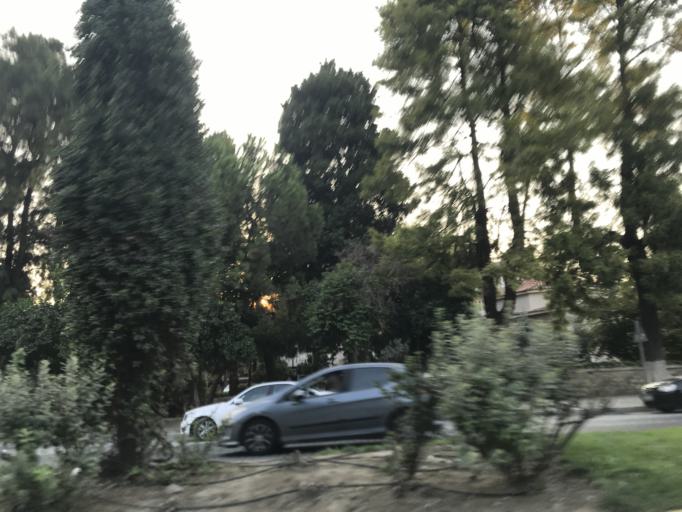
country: TR
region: Izmir
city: Selcuk
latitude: 37.9491
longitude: 27.3691
